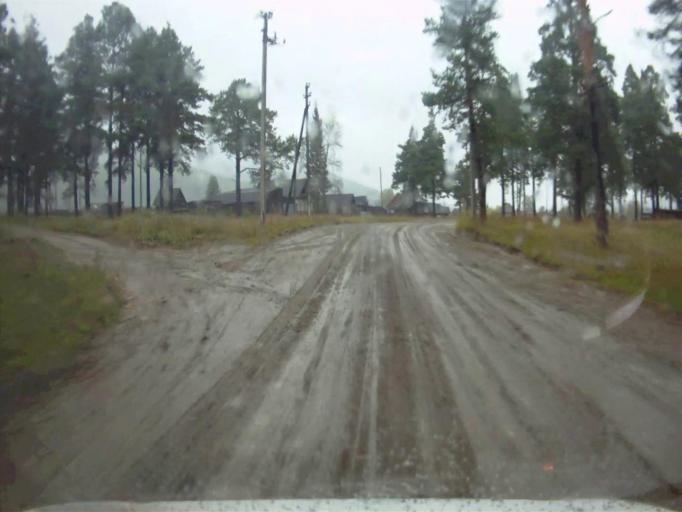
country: RU
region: Chelyabinsk
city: Kyshtym
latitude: 55.9005
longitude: 60.4658
